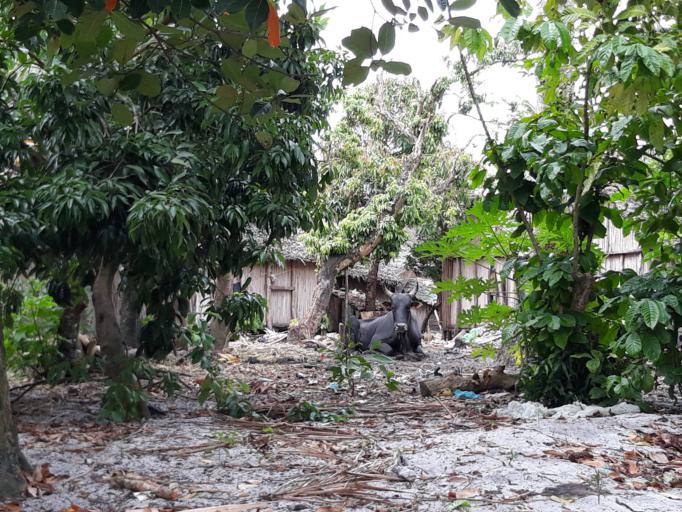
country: MG
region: Atsinanana
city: Andovoranto
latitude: -19.2567
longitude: 48.9742
